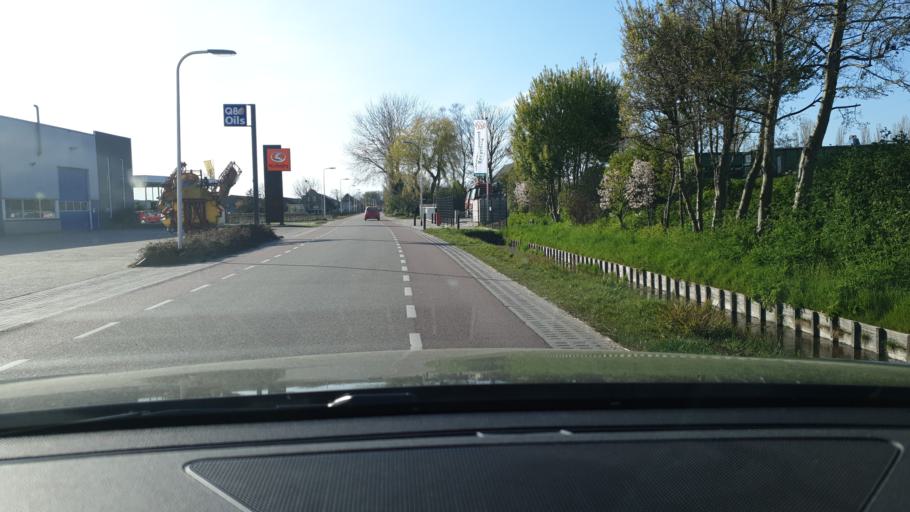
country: NL
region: South Holland
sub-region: Gemeente Noordwijkerhout
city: Noordwijkerhout
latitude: 52.2564
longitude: 4.5115
